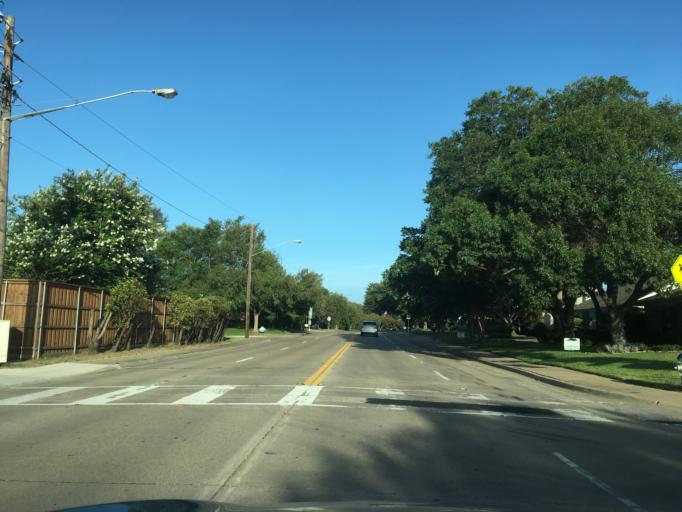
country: US
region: Texas
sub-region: Dallas County
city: Richardson
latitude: 32.8859
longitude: -96.7368
